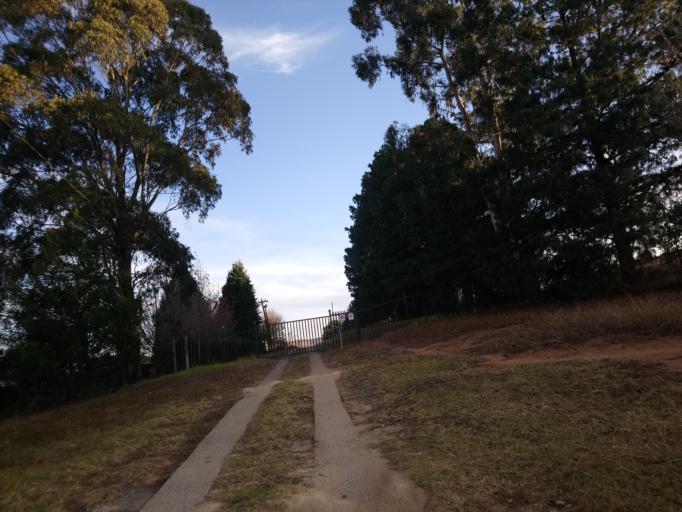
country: ZA
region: KwaZulu-Natal
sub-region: uMgungundlovu District Municipality
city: Mooirivier
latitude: -29.3284
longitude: 29.9206
